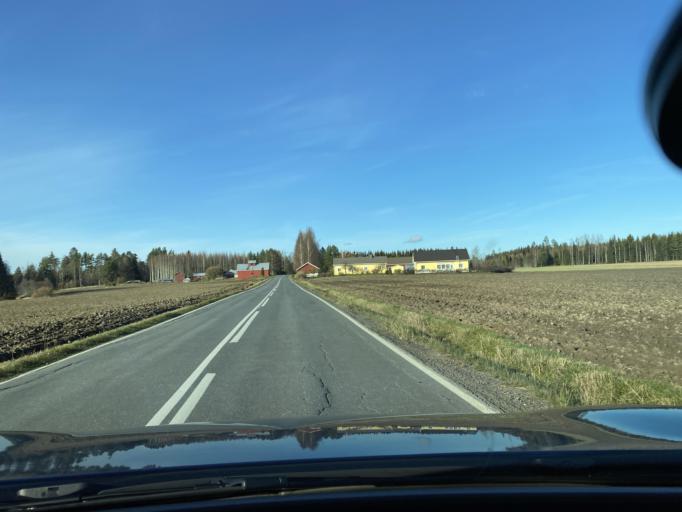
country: FI
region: Haeme
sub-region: Forssa
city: Tammela
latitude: 60.8348
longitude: 23.8388
